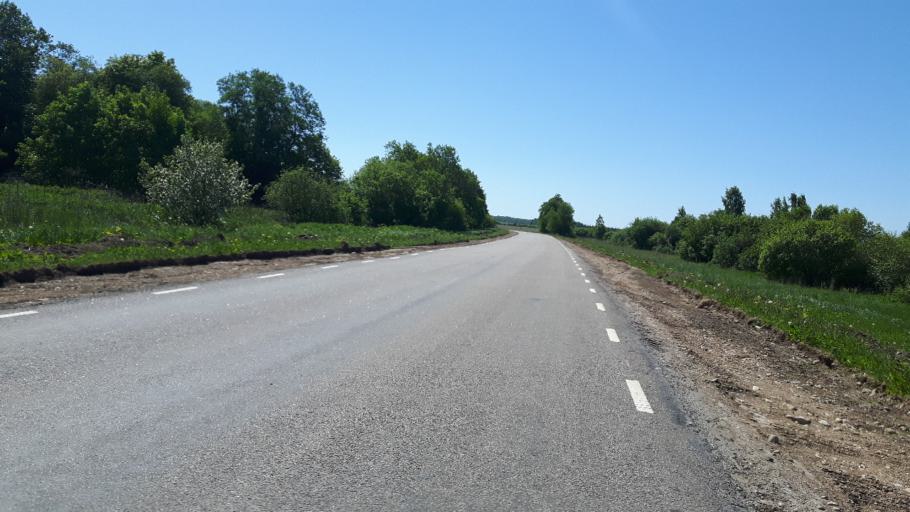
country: EE
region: Ida-Virumaa
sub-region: Narva-Joesuu linn
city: Narva-Joesuu
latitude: 59.3904
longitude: 27.9215
